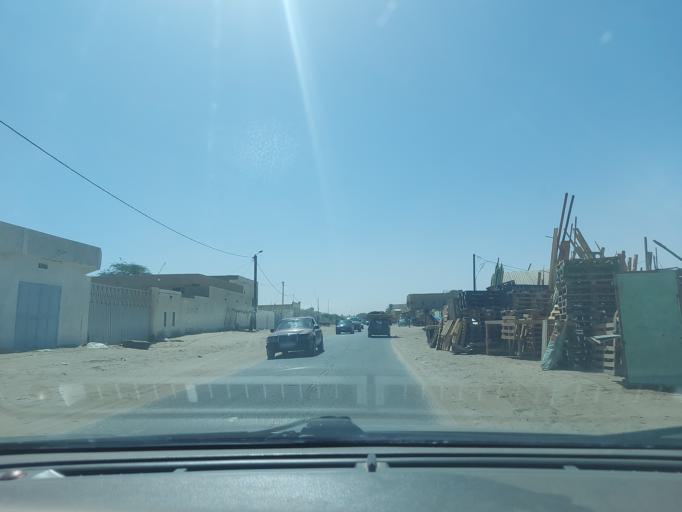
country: MR
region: Nouakchott
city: Nouakchott
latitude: 18.0622
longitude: -15.9775
